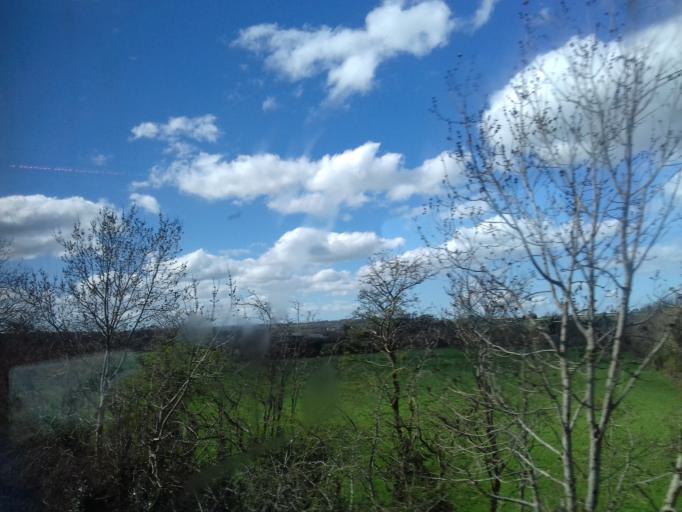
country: IE
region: Munster
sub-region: County Cork
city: Kanturk
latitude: 52.1281
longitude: -8.8842
